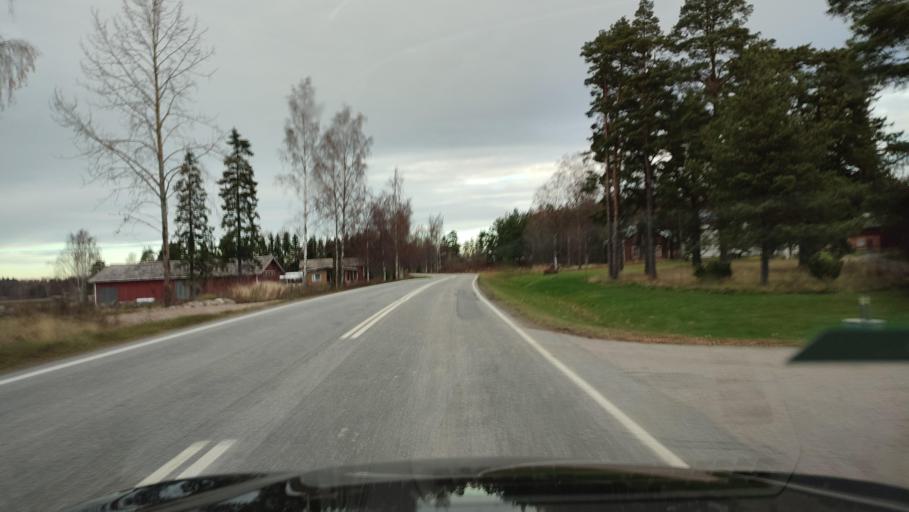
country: FI
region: Ostrobothnia
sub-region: Sydosterbotten
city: Naerpes
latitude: 62.4086
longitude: 21.3493
